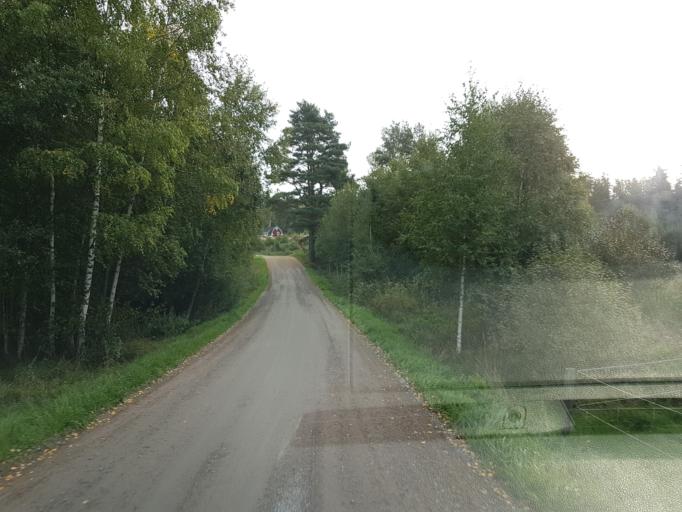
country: SE
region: OEstergoetland
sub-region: Atvidabergs Kommun
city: Atvidaberg
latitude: 58.2121
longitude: 16.0207
